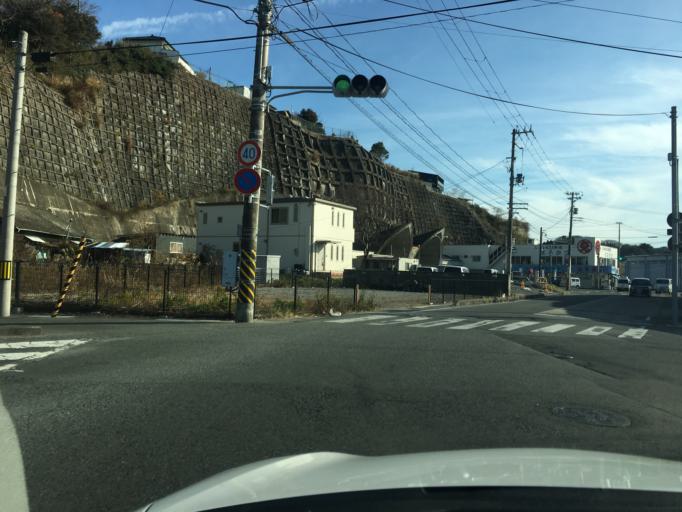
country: JP
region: Fukushima
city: Iwaki
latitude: 36.9445
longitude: 140.9142
